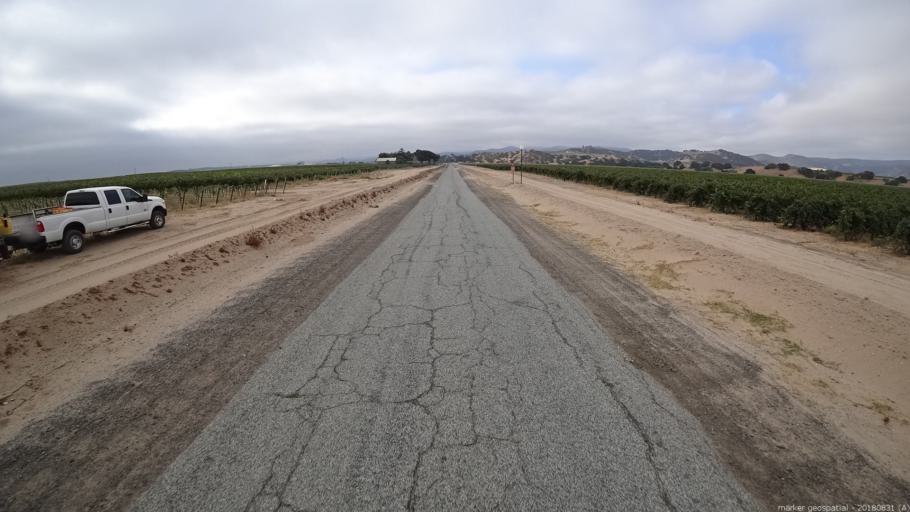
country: US
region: California
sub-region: Monterey County
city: King City
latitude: 36.1511
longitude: -121.1005
